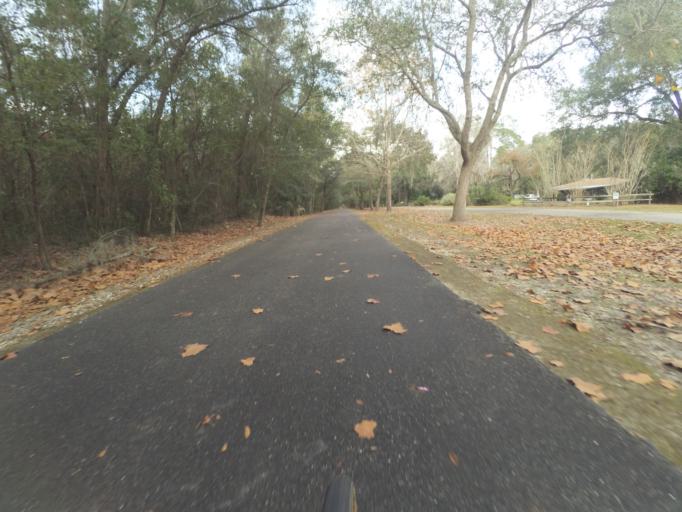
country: US
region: Florida
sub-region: Alachua County
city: Gainesville
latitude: 29.6328
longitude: -82.3129
